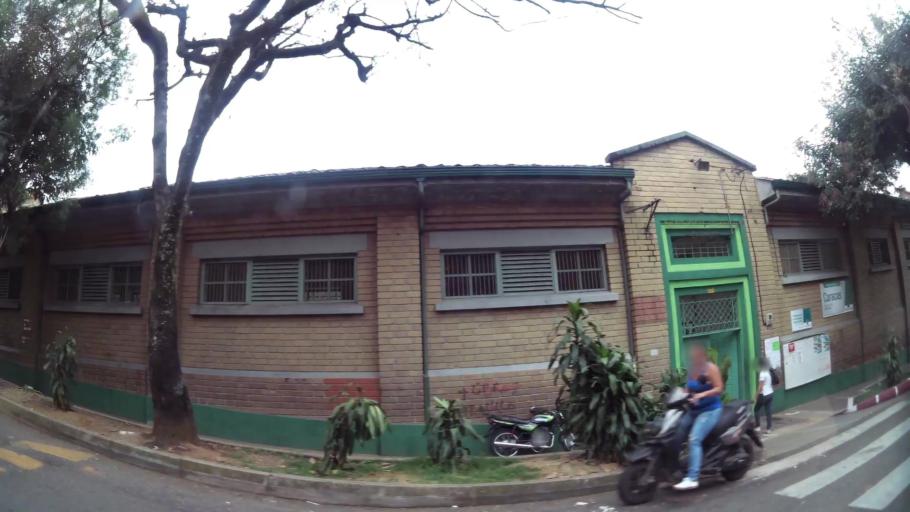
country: CO
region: Antioquia
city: Medellin
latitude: 6.2453
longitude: -75.5539
